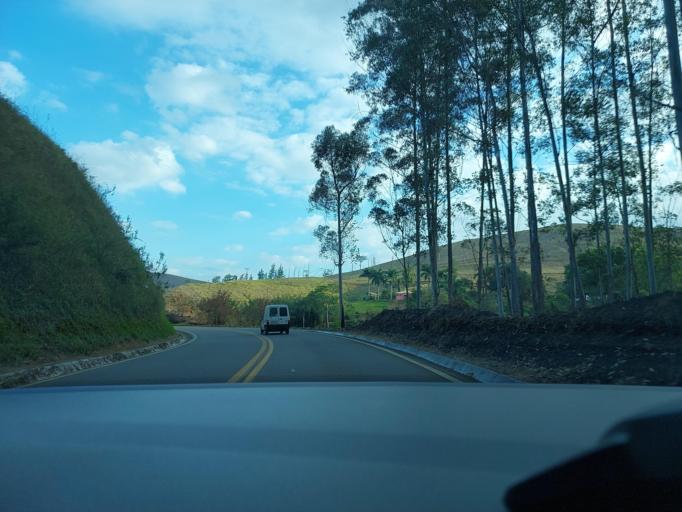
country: BR
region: Minas Gerais
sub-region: Muriae
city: Muriae
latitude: -21.0689
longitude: -42.5066
